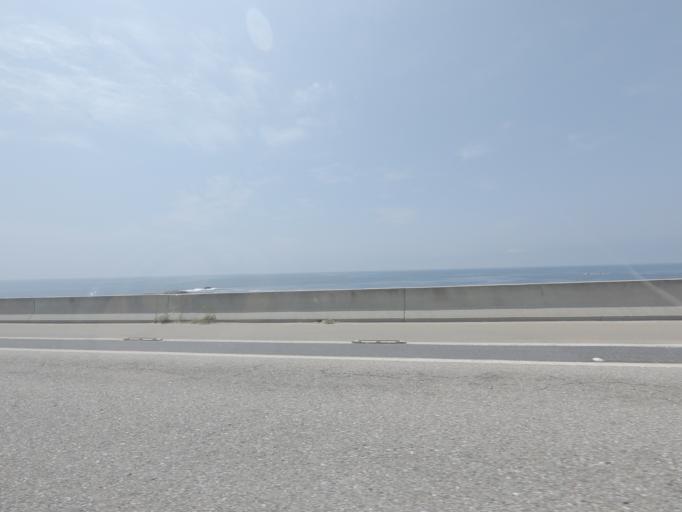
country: ES
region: Galicia
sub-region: Provincia de Pontevedra
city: Baiona
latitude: 42.1058
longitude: -8.8974
